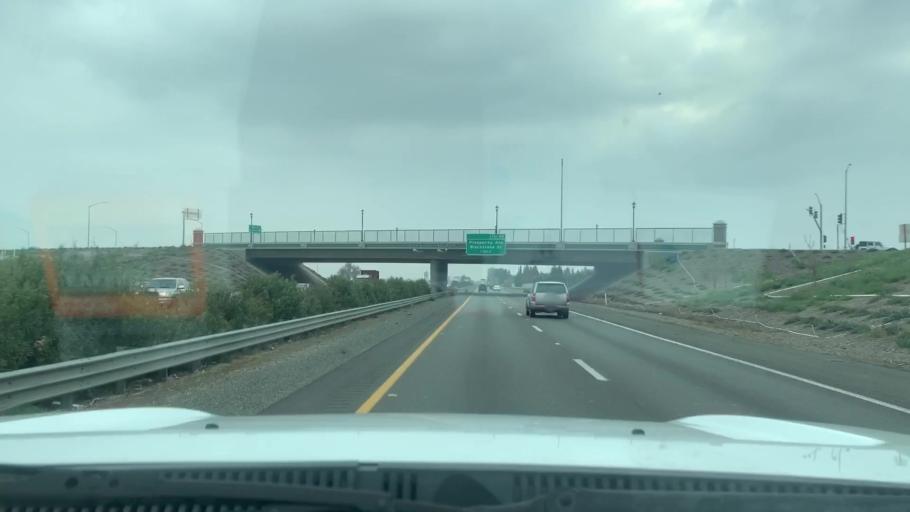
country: US
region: California
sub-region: Tulare County
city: Tulare
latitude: 36.2412
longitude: -119.3464
